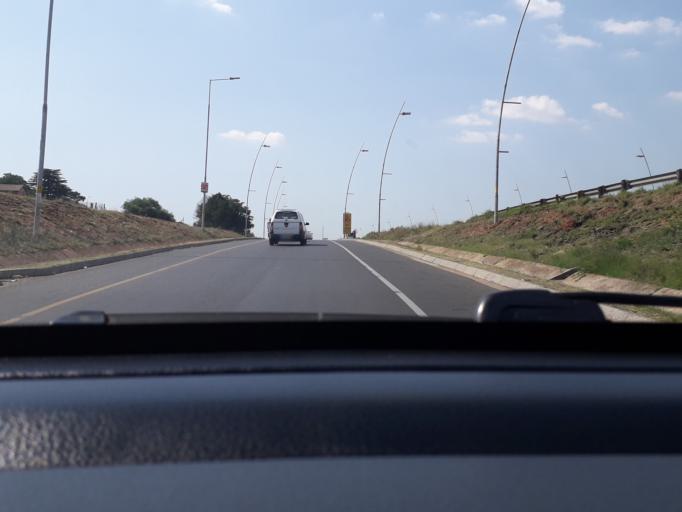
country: ZA
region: Gauteng
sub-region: City of Johannesburg Metropolitan Municipality
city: Modderfontein
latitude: -26.0879
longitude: 28.1904
